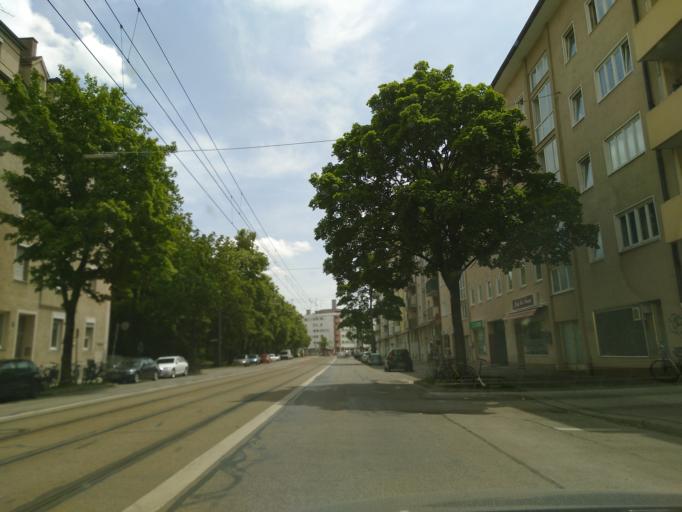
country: DE
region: Bavaria
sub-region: Upper Bavaria
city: Munich
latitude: 48.1164
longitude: 11.5910
